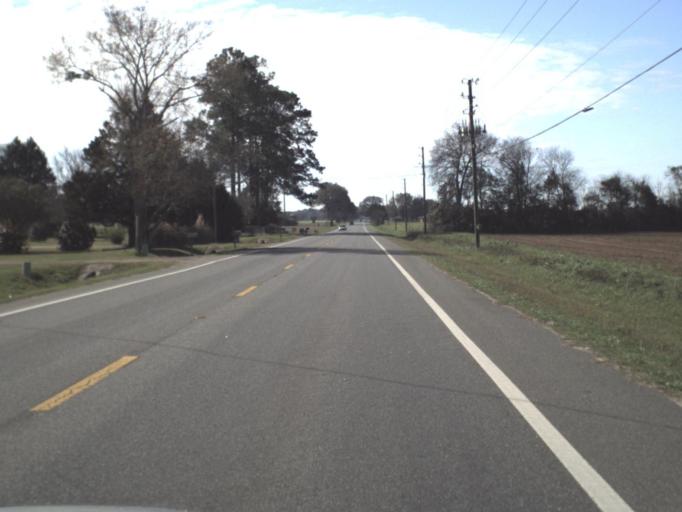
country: US
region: Florida
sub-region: Jackson County
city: Malone
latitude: 30.8573
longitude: -85.1638
